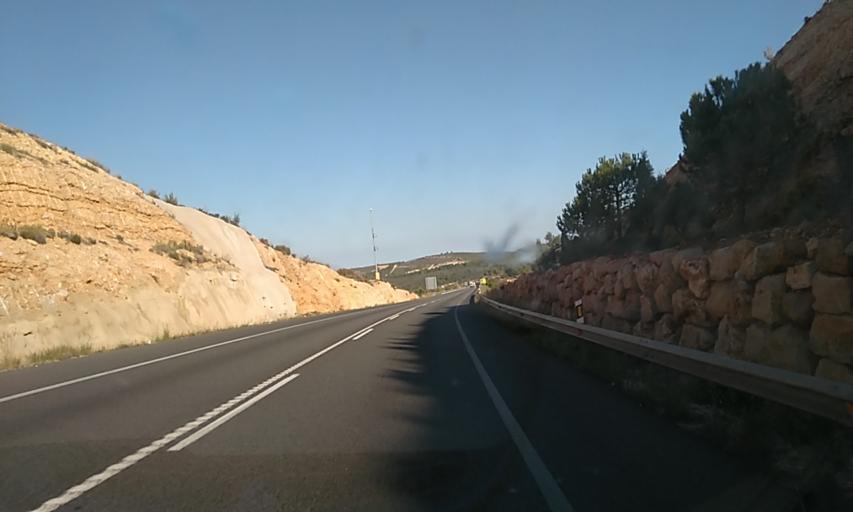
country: ES
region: Valencia
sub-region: Provincia de Castello
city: Torreblanca
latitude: 40.2114
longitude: 0.1250
